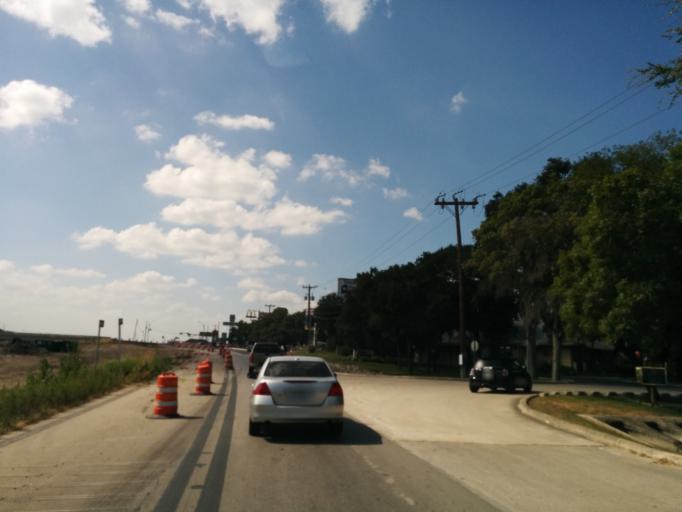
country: US
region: Texas
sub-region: Bexar County
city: Cross Mountain
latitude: 29.6742
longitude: -98.6341
